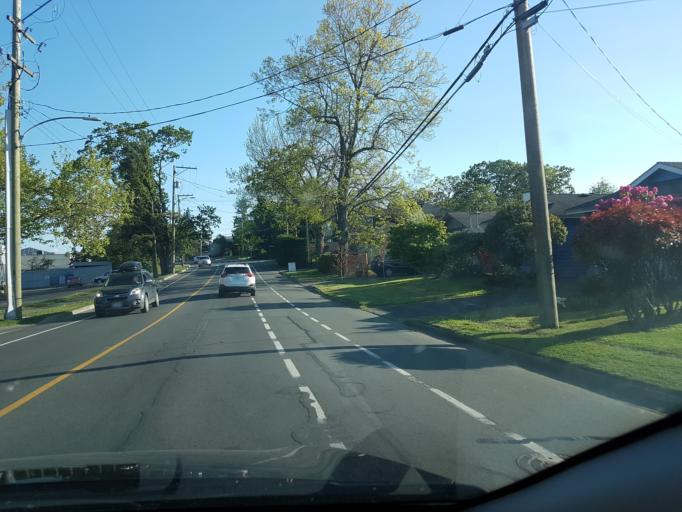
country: CA
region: British Columbia
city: Oak Bay
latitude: 48.4726
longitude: -123.3346
